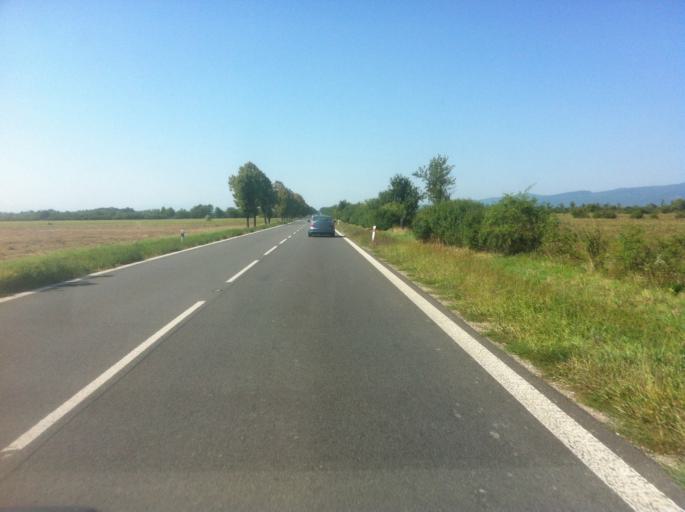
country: SK
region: Kosicky
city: Sobrance
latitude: 48.7562
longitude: 22.1451
